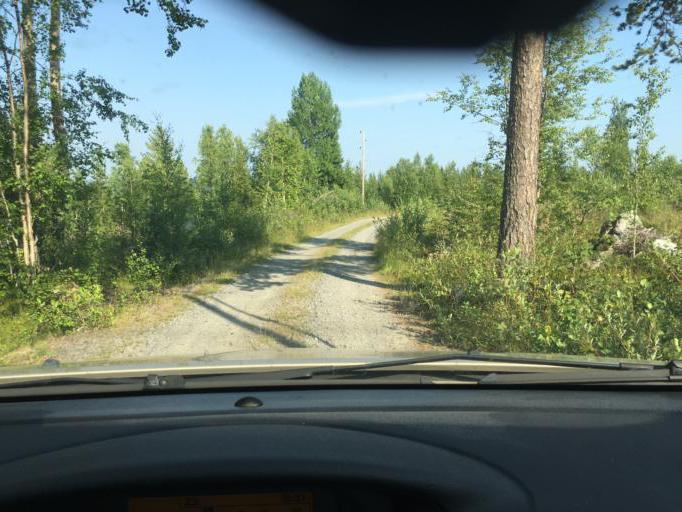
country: SE
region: Norrbotten
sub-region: Kalix Kommun
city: Toere
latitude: 65.8694
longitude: 22.6431
